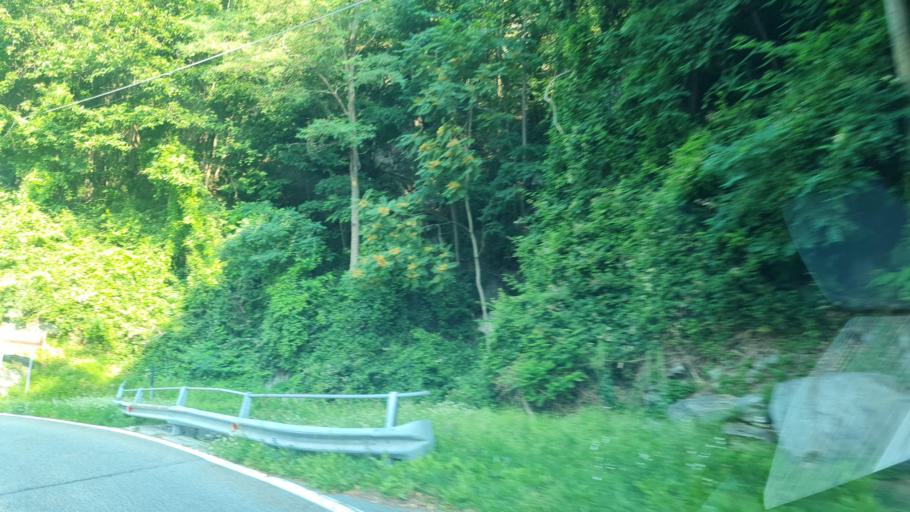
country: IT
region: Aosta Valley
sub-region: Valle d'Aosta
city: Pont-Bozet
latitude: 45.6109
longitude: 7.7085
